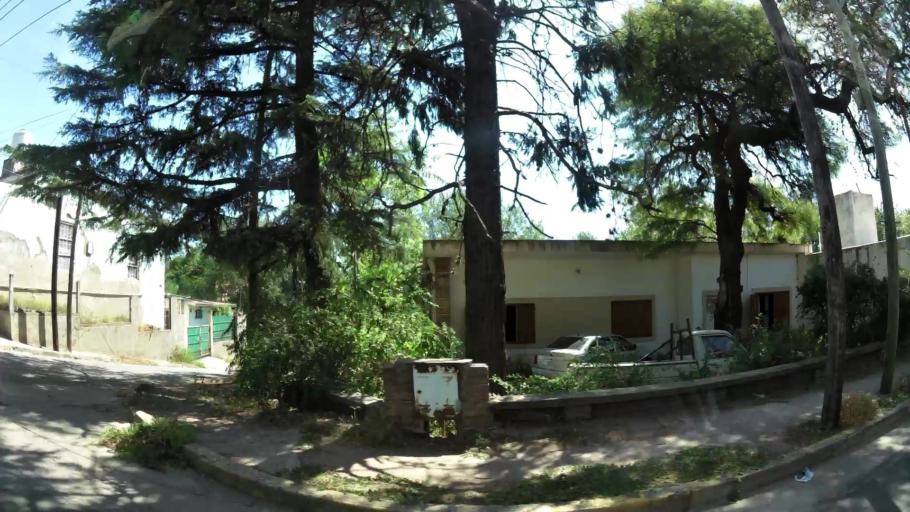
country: AR
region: Cordoba
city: Villa Allende
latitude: -31.2980
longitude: -64.3012
